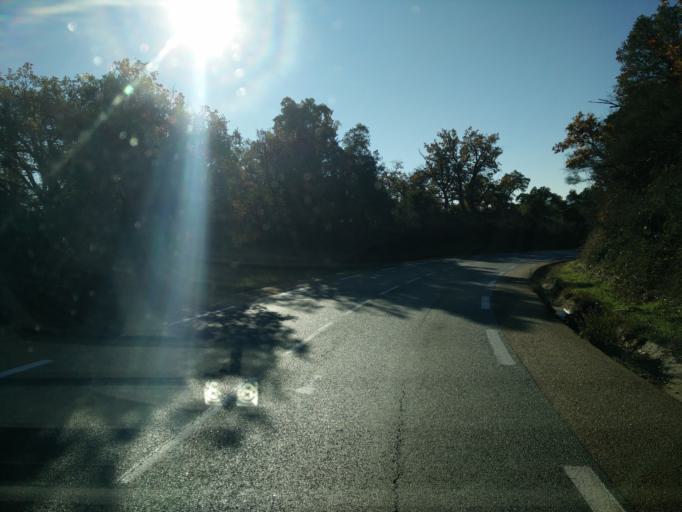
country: FR
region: Provence-Alpes-Cote d'Azur
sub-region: Departement du Var
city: La Garde-Freinet
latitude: 43.2989
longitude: 6.4923
